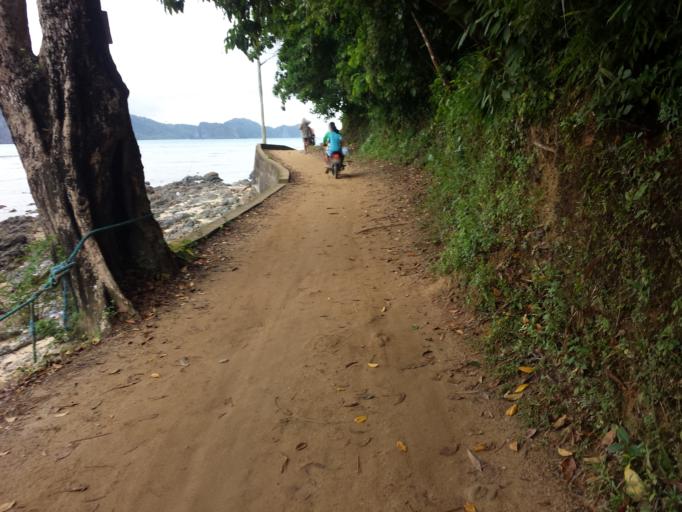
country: PH
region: Mimaropa
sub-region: Province of Palawan
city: El Nido
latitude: 11.1852
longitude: 119.3925
